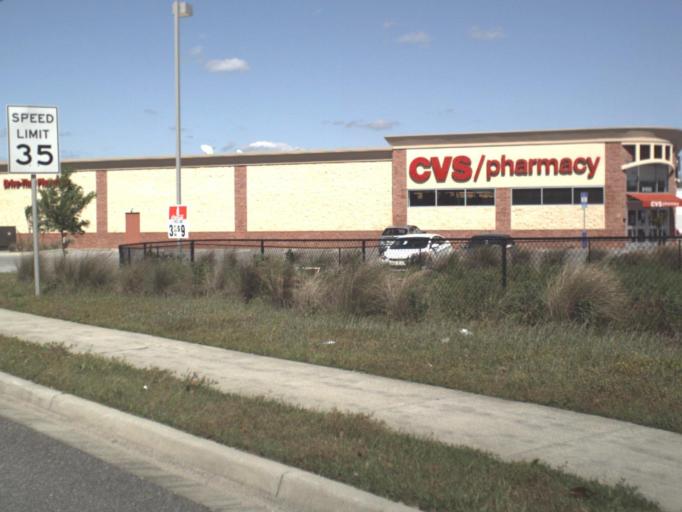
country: US
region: Florida
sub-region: Escambia County
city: Ferry Pass
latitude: 30.5107
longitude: -87.2201
